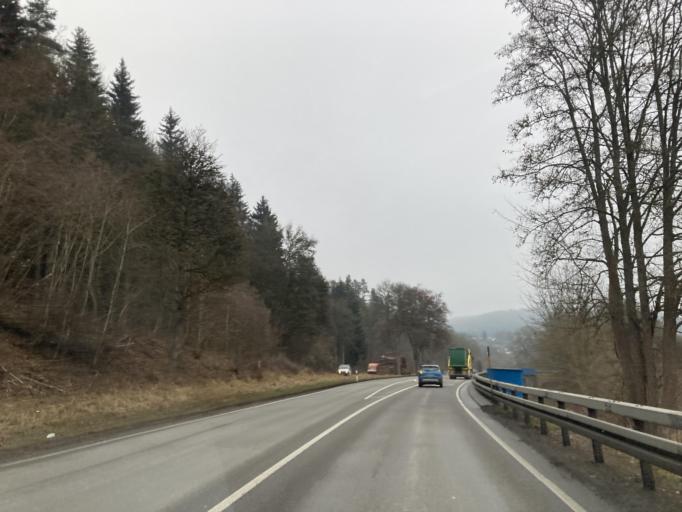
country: DE
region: Baden-Wuerttemberg
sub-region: Freiburg Region
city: Immendingen
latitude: 47.9497
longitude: 8.7554
